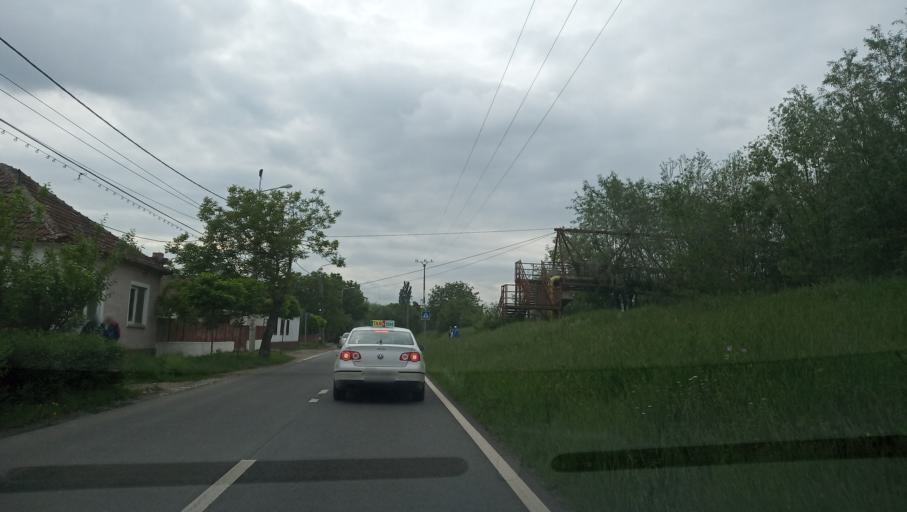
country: RO
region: Timis
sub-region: Comuna Ghiroda
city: Ghiroda
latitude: 45.7544
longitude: 21.2770
